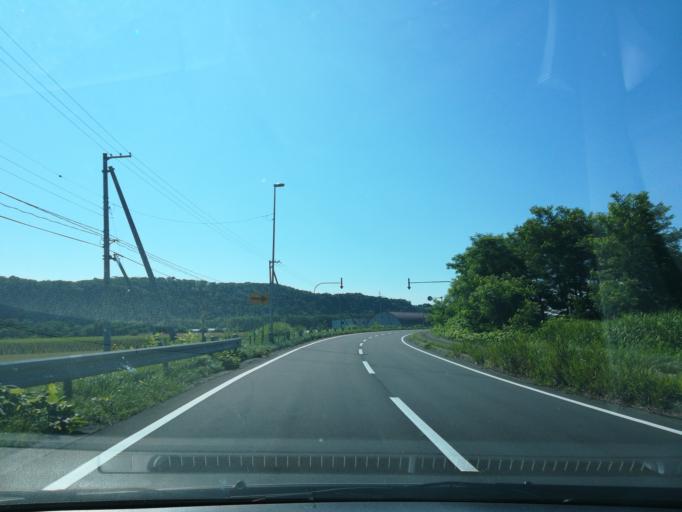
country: JP
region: Hokkaido
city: Chitose
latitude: 42.9082
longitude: 141.9287
